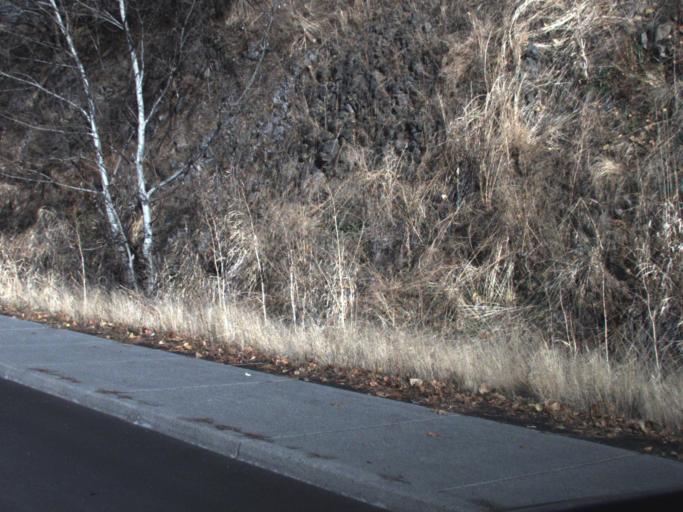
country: US
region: Washington
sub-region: Whitman County
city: Pullman
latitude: 46.7248
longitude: -117.1657
